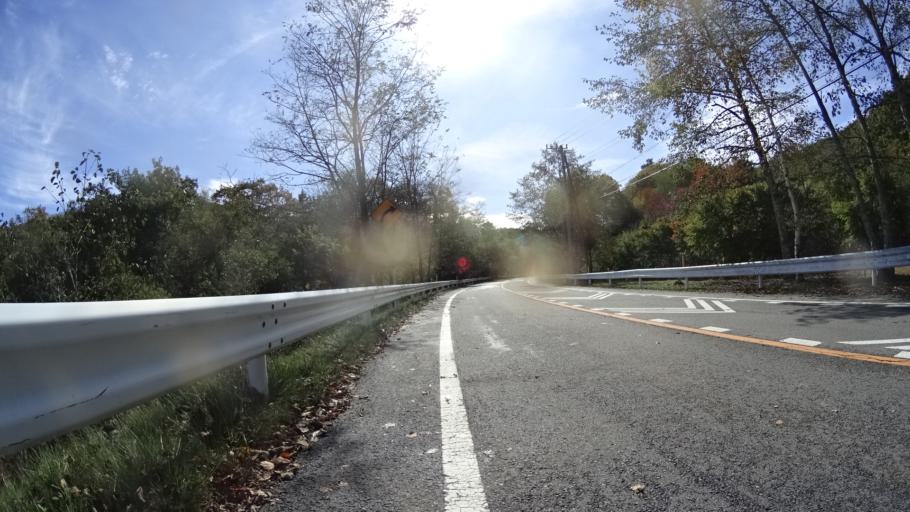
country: JP
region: Yamanashi
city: Enzan
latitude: 35.7854
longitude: 138.8006
